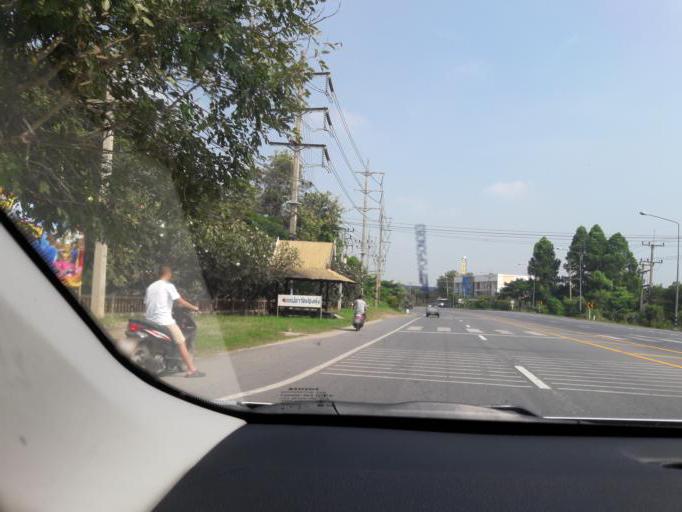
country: TH
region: Ang Thong
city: Ang Thong
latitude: 14.5696
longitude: 100.4537
